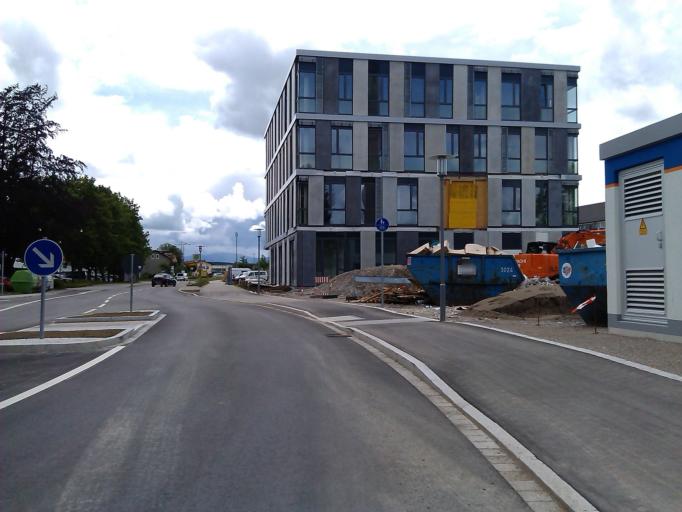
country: DE
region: Bavaria
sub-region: Swabia
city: Marktoberdorf
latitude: 47.7834
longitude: 10.6155
